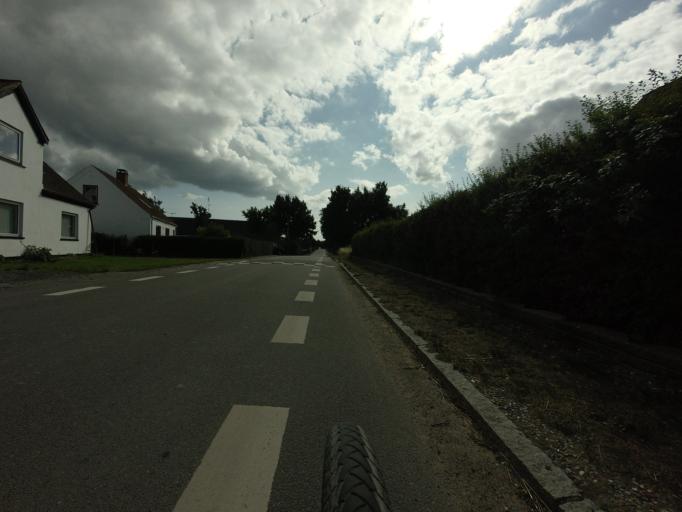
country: DK
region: Zealand
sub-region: Vordingborg Kommune
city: Stege
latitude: 55.0014
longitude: 12.3138
